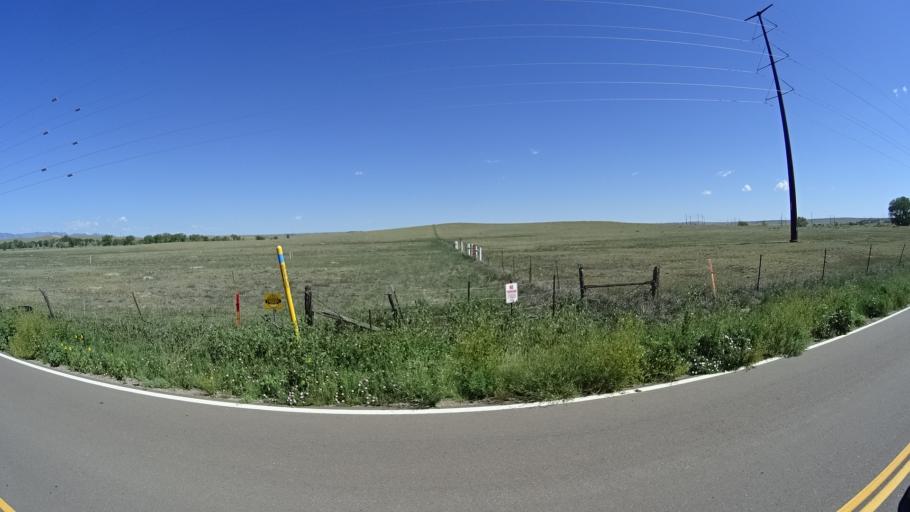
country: US
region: Colorado
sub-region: El Paso County
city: Security-Widefield
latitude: 38.7810
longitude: -104.6412
